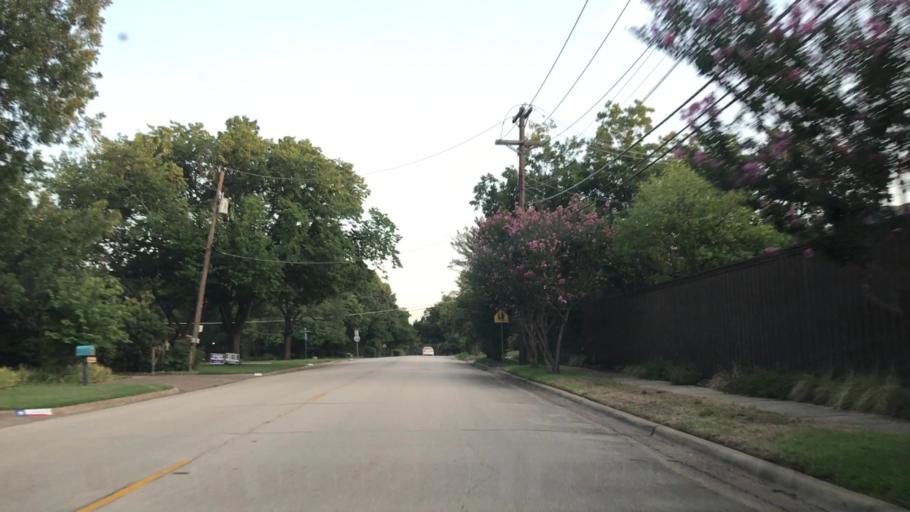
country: US
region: Texas
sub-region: Dallas County
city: University Park
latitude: 32.9015
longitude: -96.7803
